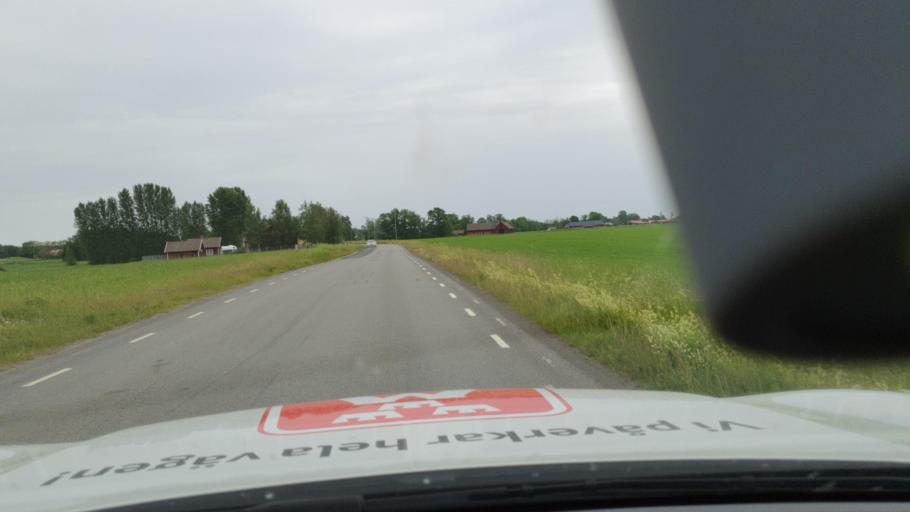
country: SE
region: Vaestra Goetaland
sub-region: Tidaholms Kommun
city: Olofstorp
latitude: 58.3431
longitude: 13.9702
